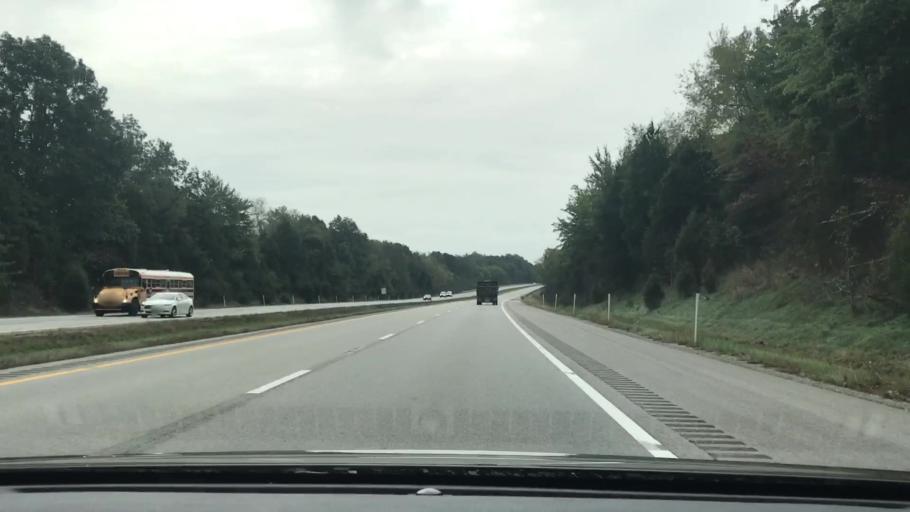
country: US
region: Kentucky
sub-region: Barren County
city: Cave City
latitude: 37.0440
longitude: -86.0713
